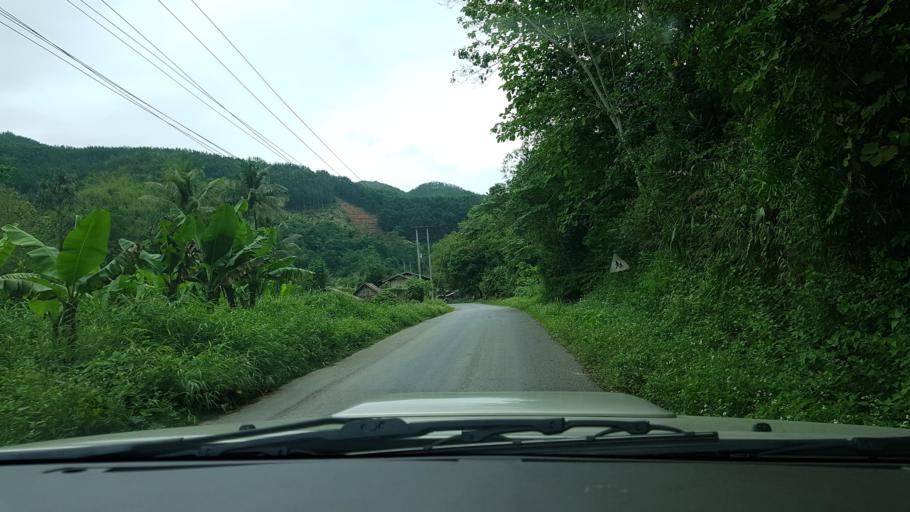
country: LA
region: Phongsali
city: Khoa
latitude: 21.0696
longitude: 102.3783
